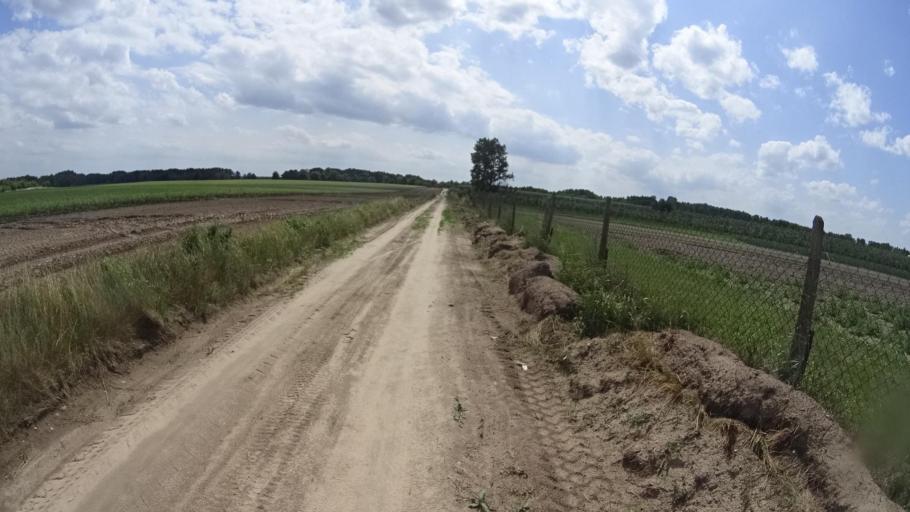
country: PL
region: Masovian Voivodeship
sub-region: Powiat grojecki
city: Goszczyn
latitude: 51.7003
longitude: 20.8246
